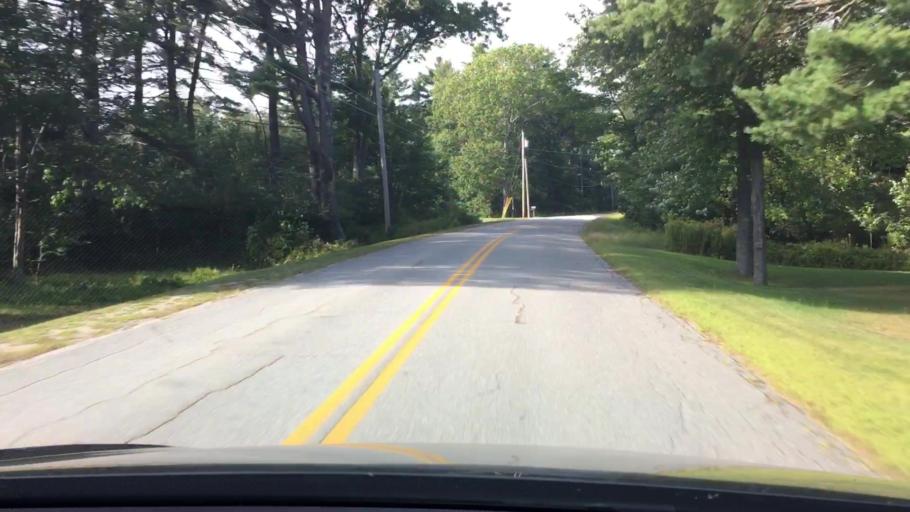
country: US
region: Maine
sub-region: Hancock County
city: Orland
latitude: 44.5227
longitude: -68.7642
